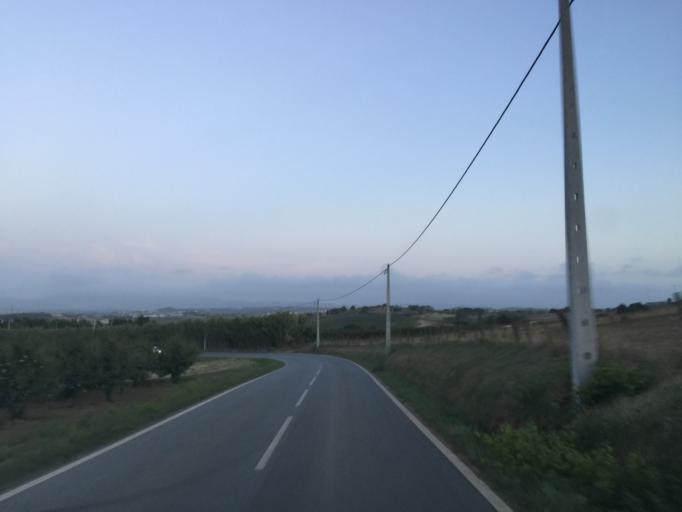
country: PT
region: Leiria
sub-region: Bombarral
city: Bombarral
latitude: 39.2758
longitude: -9.1849
